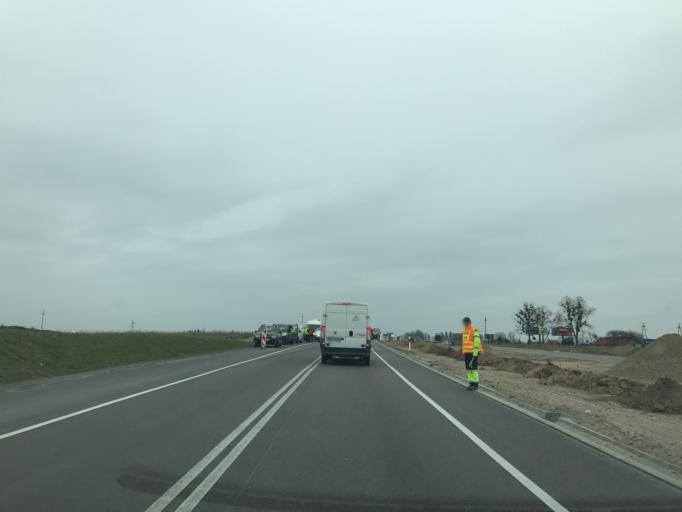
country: PL
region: Warmian-Masurian Voivodeship
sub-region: Powiat olsztynski
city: Olsztynek
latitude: 53.6180
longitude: 20.3352
